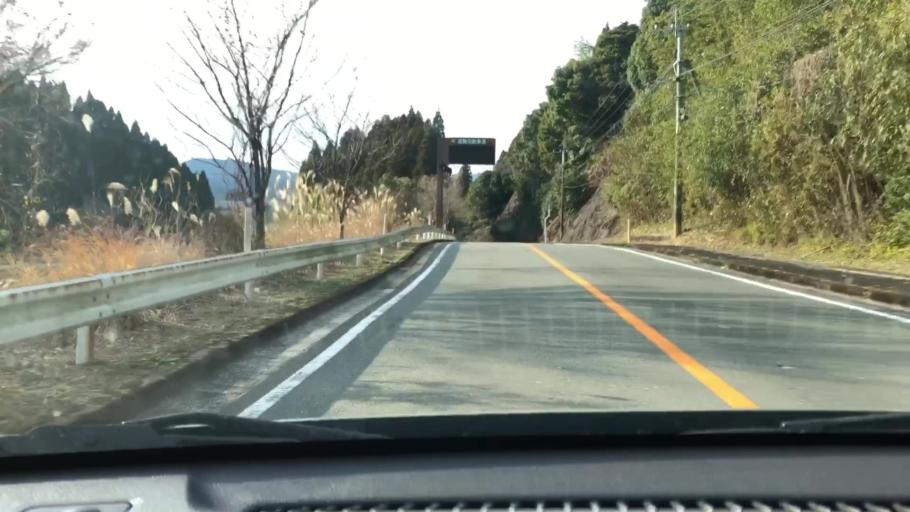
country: JP
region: Miyazaki
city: Miyazaki-shi
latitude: 31.8187
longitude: 131.3002
